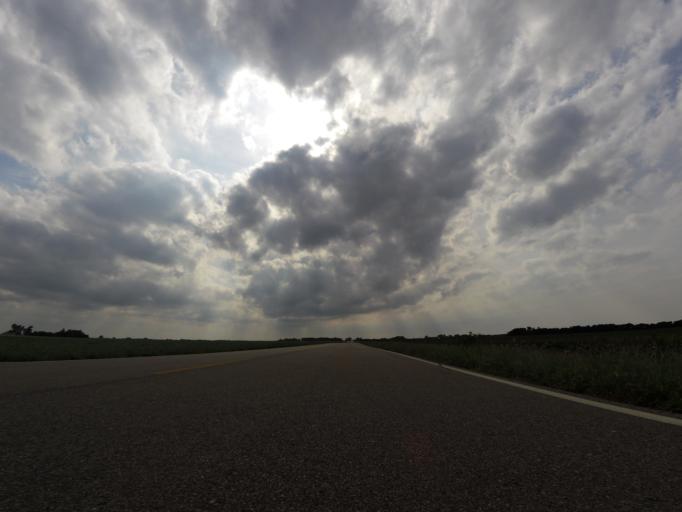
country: US
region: Kansas
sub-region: Reno County
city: South Hutchinson
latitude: 37.8975
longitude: -98.0418
